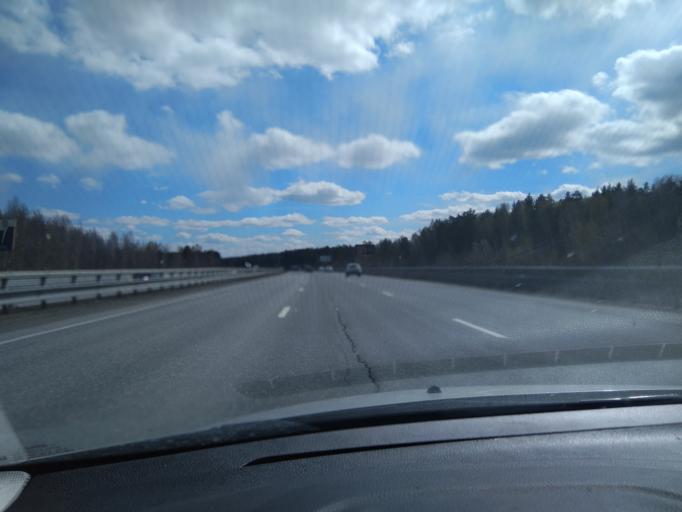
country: RU
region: Sverdlovsk
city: Shuvakish
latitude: 56.9190
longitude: 60.5081
